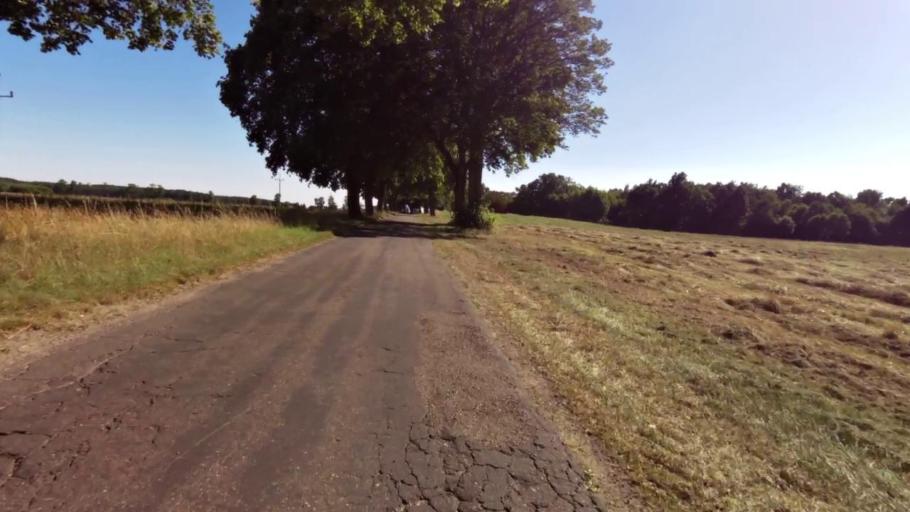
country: PL
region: West Pomeranian Voivodeship
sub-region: Powiat szczecinecki
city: Szczecinek
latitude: 53.7776
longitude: 16.6770
